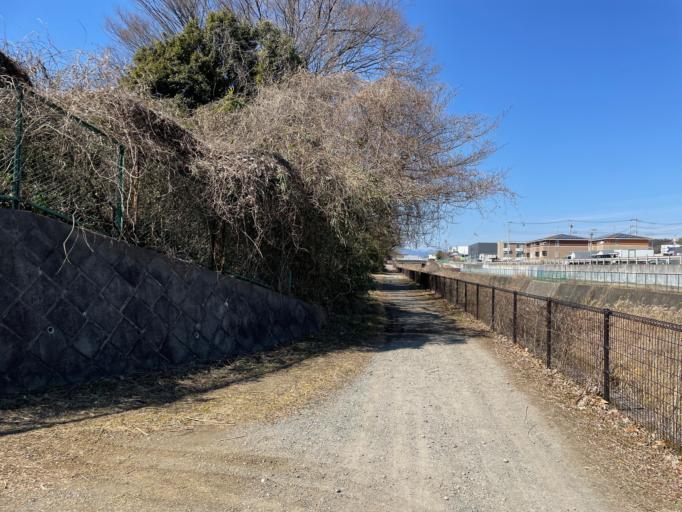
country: JP
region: Tokyo
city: Hachioji
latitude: 35.6821
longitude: 139.3479
